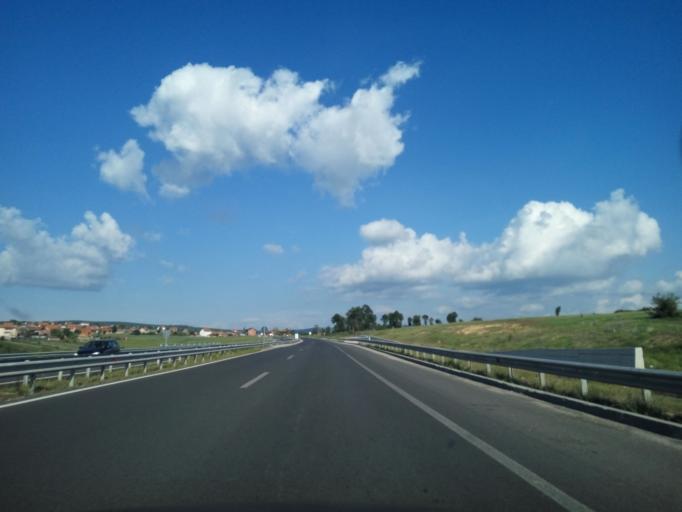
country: XK
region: Prizren
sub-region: Komuna e Malisheves
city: Llazice
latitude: 42.5674
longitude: 20.7455
